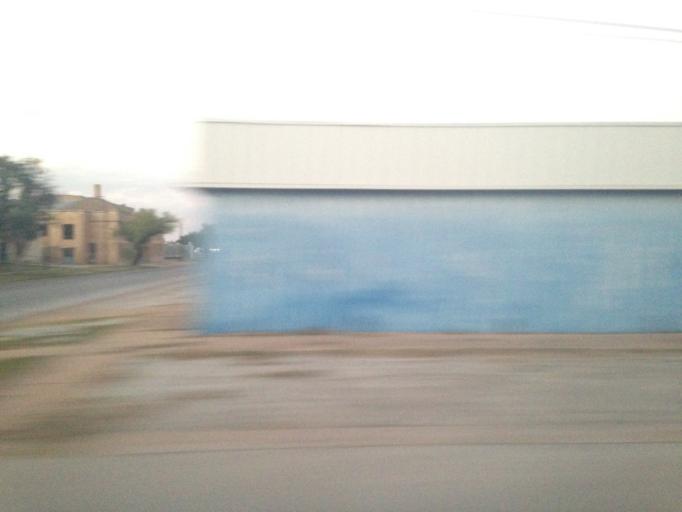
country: US
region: Texas
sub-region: Taylor County
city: Abilene
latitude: 32.4471
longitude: -99.7414
